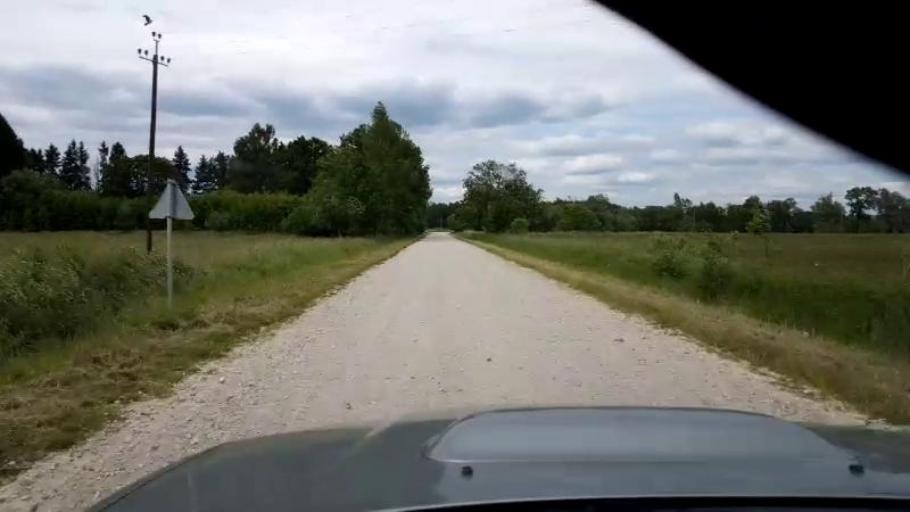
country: EE
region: Paernumaa
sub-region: Sauga vald
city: Sauga
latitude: 58.5132
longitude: 24.5807
